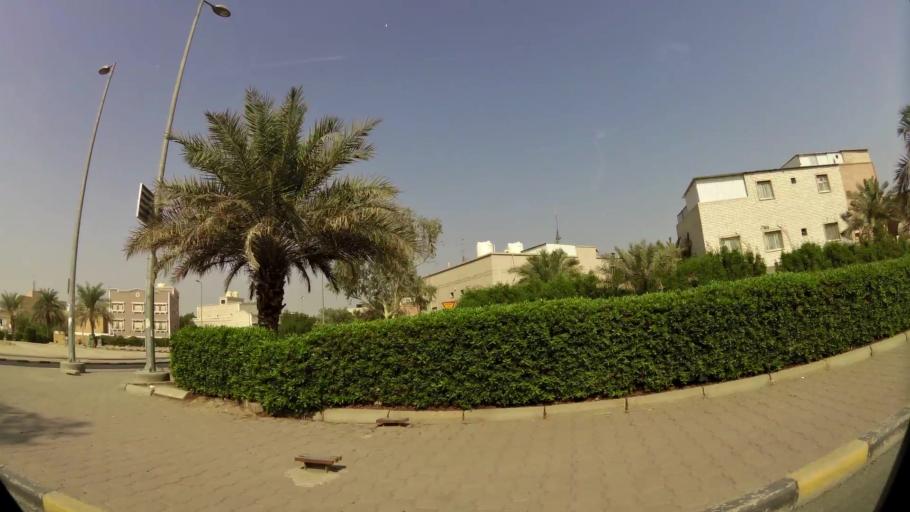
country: KW
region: Al Asimah
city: Ar Rabiyah
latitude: 29.2819
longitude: 47.8903
